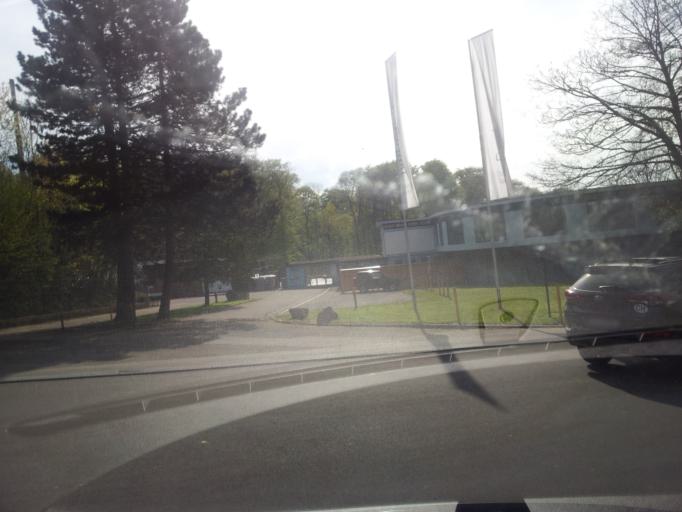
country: CH
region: Zurich
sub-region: Bezirk Zuerich
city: Zuerich (Kreis 7)
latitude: 47.3761
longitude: 8.5774
